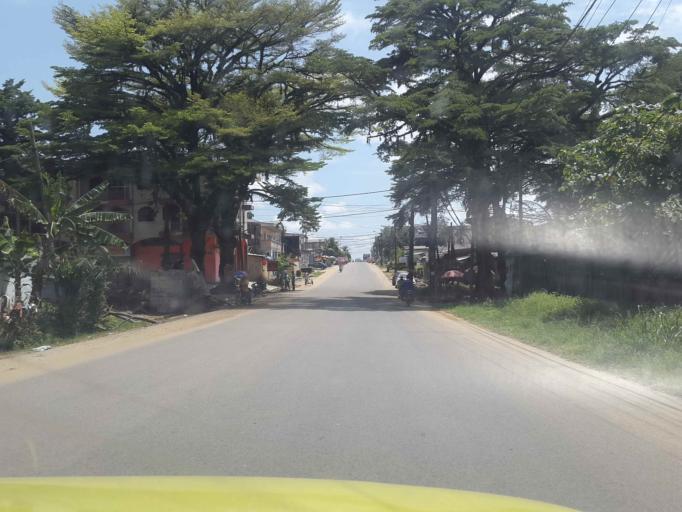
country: CM
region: Littoral
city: Douala
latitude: 4.0893
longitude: 9.7466
